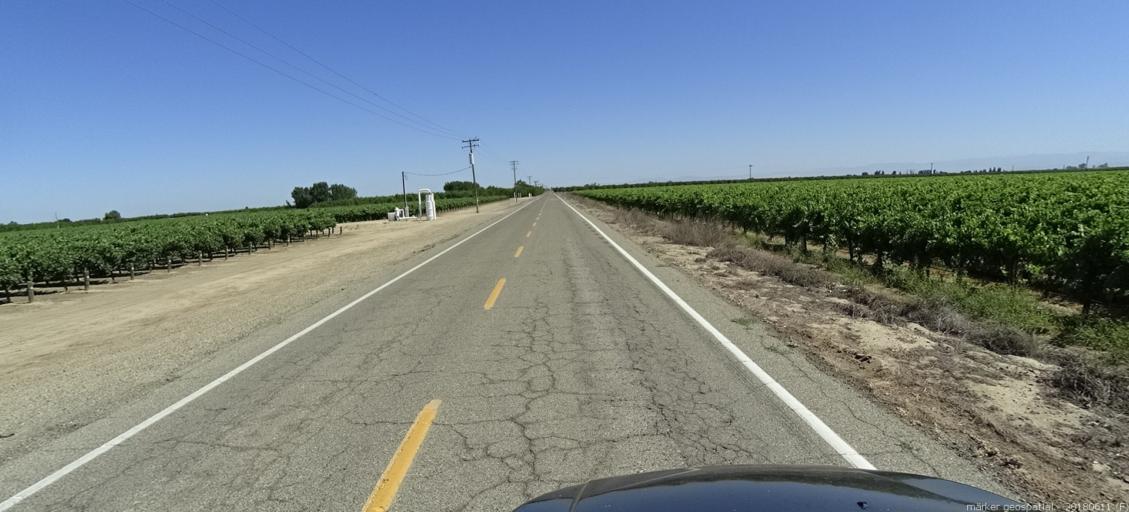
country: US
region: California
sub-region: Madera County
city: Fairmead
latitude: 36.9794
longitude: -120.2023
